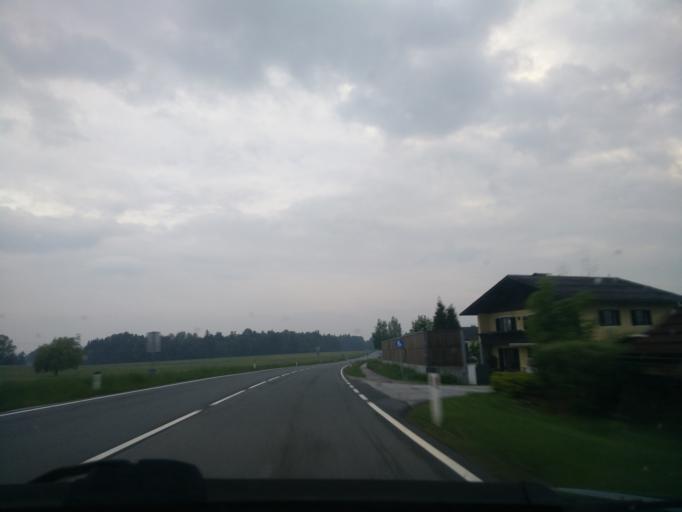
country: AT
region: Salzburg
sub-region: Politischer Bezirk Salzburg-Umgebung
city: Elixhausen
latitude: 47.8974
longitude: 13.0779
